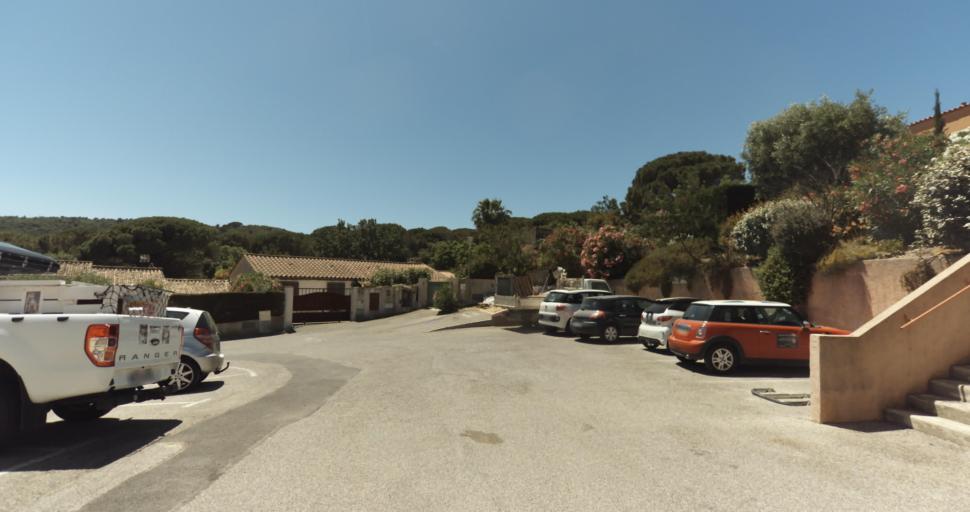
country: FR
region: Provence-Alpes-Cote d'Azur
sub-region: Departement du Var
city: Gassin
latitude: 43.2457
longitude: 6.5669
